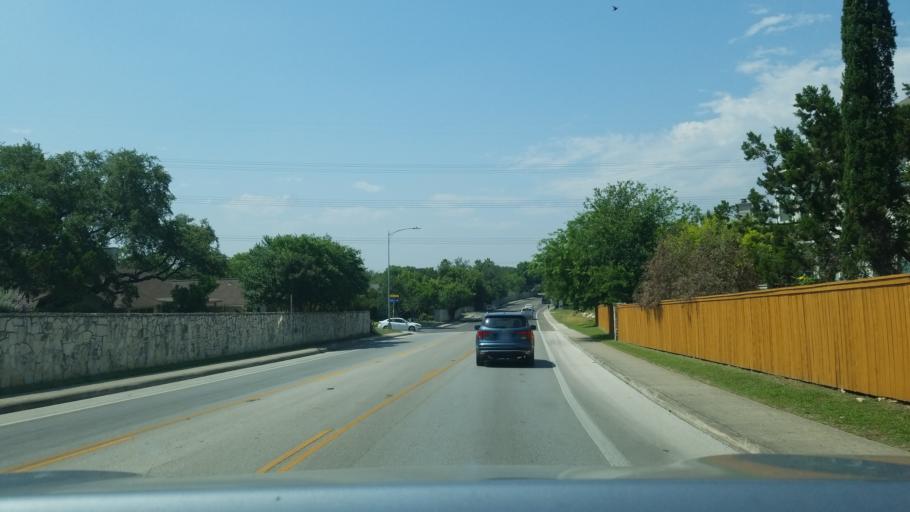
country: US
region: Texas
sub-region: Bexar County
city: Hollywood Park
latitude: 29.6340
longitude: -98.4444
